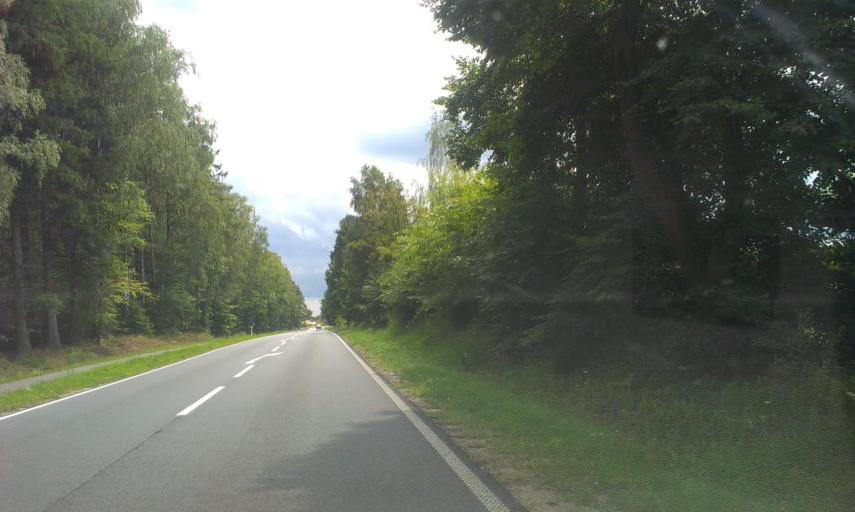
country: PL
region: West Pomeranian Voivodeship
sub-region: Koszalin
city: Koszalin
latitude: 54.0773
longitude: 16.1619
